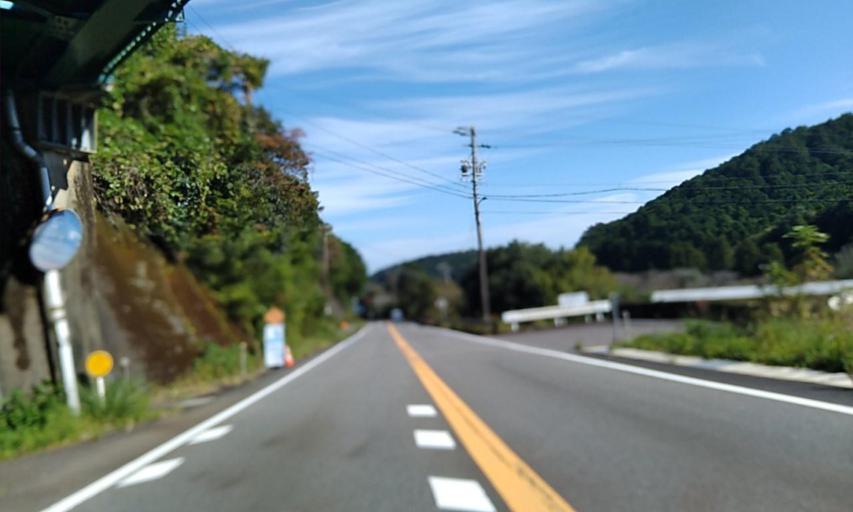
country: JP
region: Mie
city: Owase
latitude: 34.1599
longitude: 136.2726
